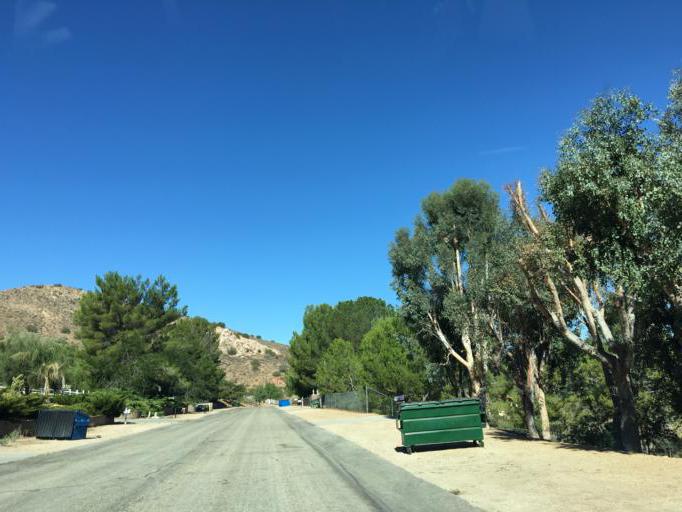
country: US
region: California
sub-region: Los Angeles County
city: Acton
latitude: 34.4620
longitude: -118.1737
